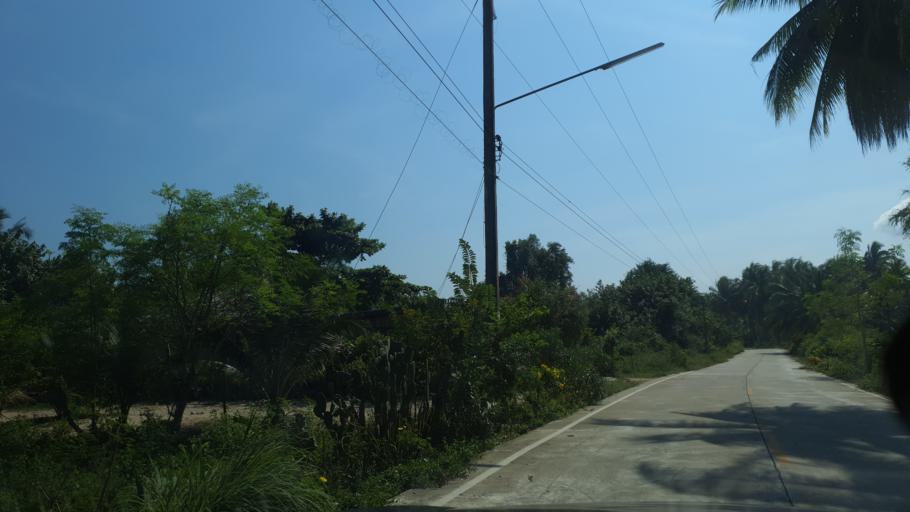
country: TH
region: Surat Thani
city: Tha Chana
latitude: 9.5988
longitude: 99.2058
